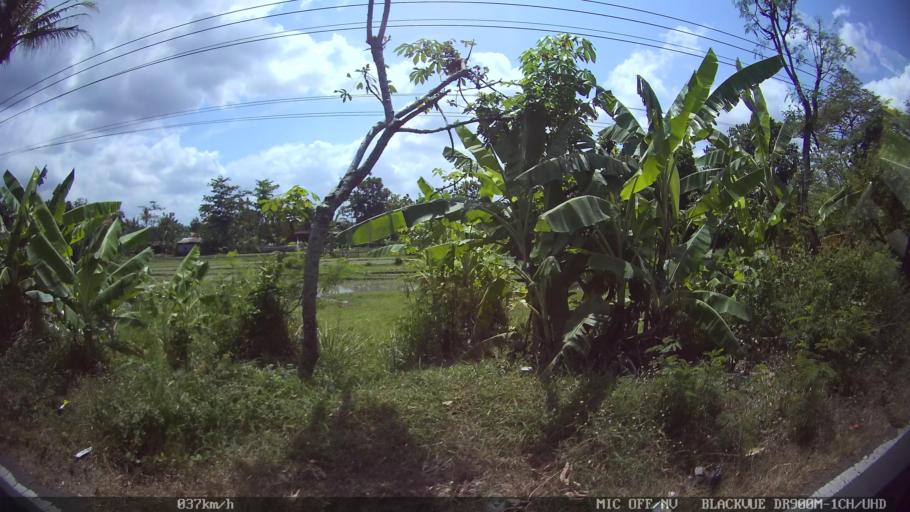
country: ID
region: Daerah Istimewa Yogyakarta
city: Bantul
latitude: -7.9052
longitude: 110.3359
